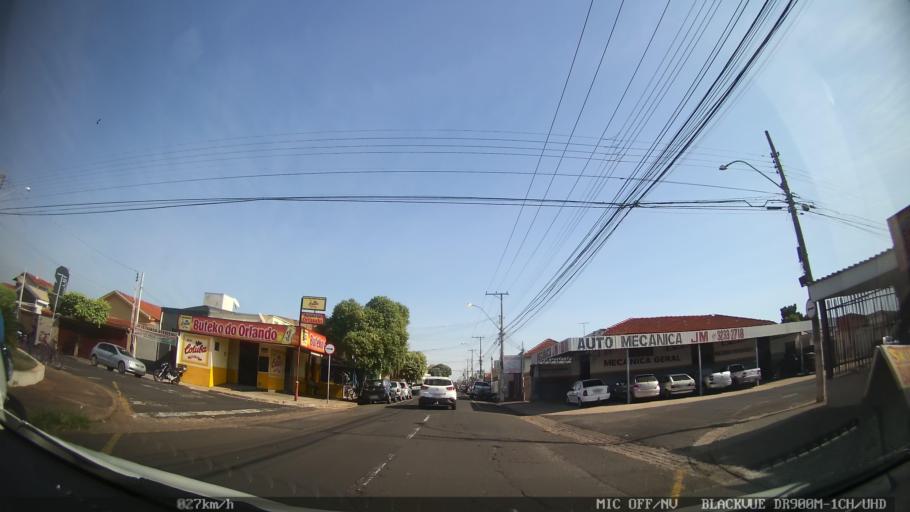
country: BR
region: Sao Paulo
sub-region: Sao Jose Do Rio Preto
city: Sao Jose do Rio Preto
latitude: -20.7981
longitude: -49.3870
